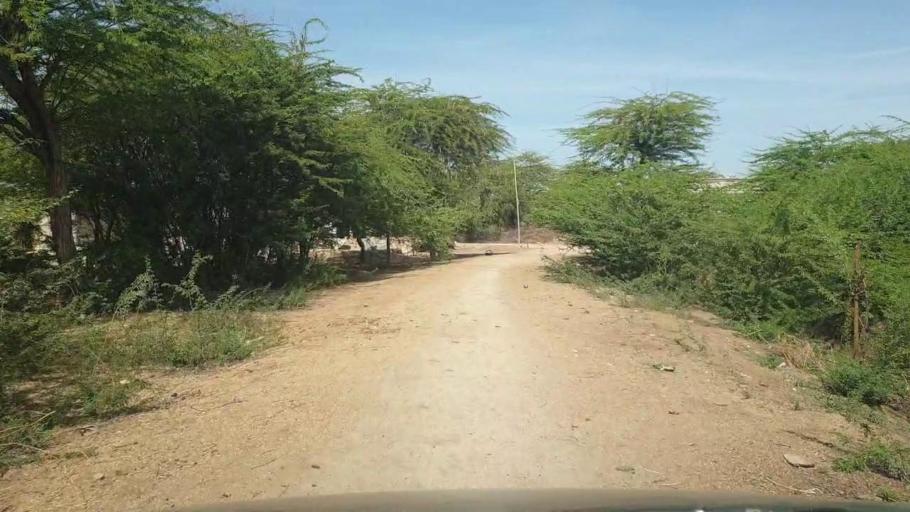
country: PK
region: Sindh
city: Kunri
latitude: 25.3103
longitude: 69.5767
